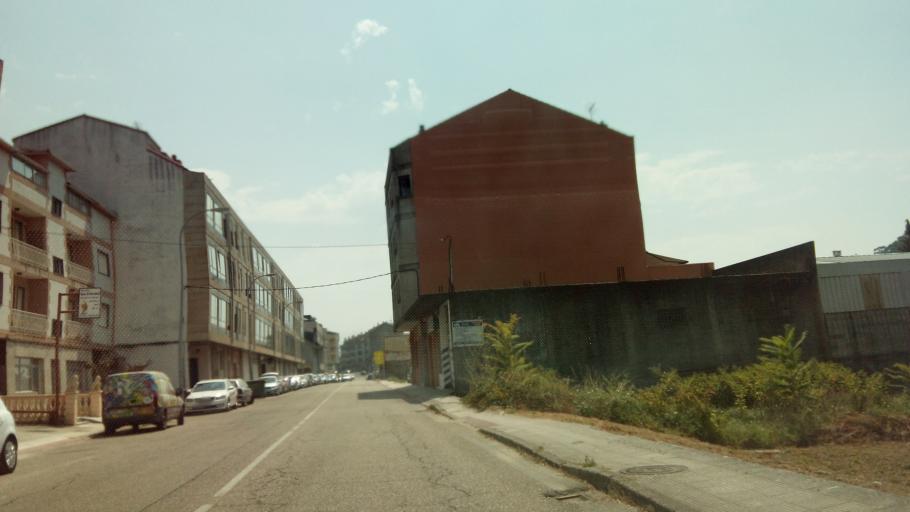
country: ES
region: Galicia
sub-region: Provincia de Pontevedra
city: Tui
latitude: 42.0539
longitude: -8.6522
